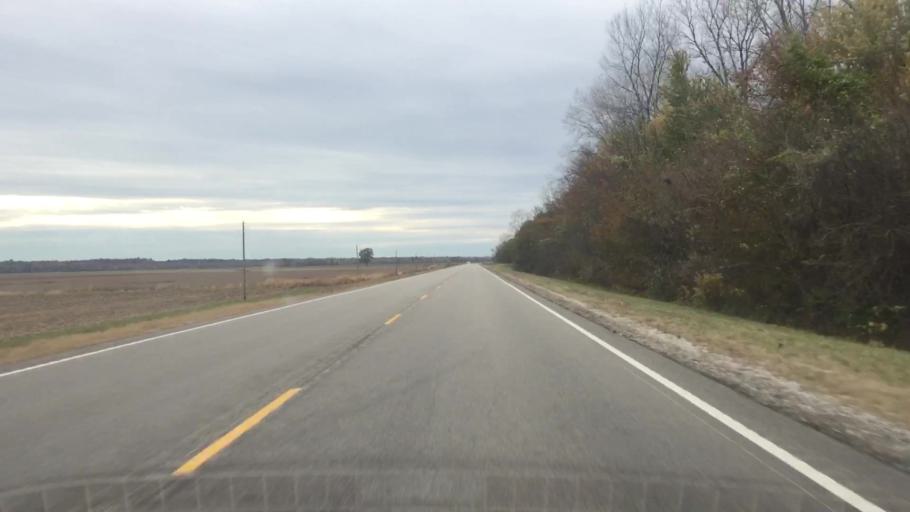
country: US
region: Missouri
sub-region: Callaway County
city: Holts Summit
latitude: 38.5816
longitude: -92.0717
